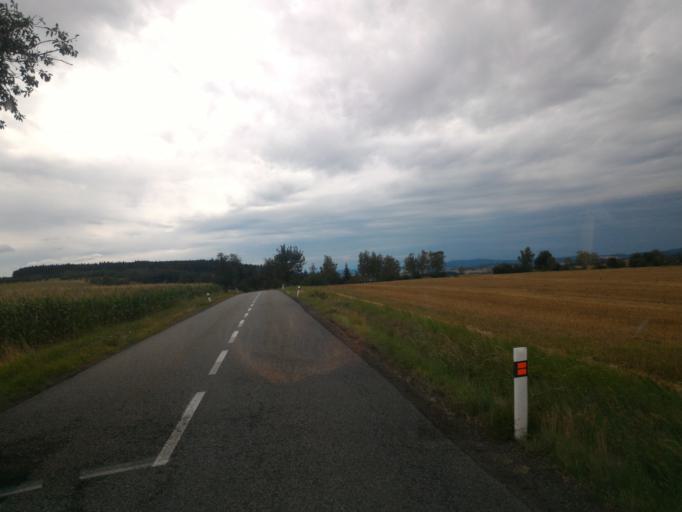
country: CZ
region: Vysocina
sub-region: Okres Jihlava
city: Trest'
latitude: 49.2307
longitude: 15.5396
